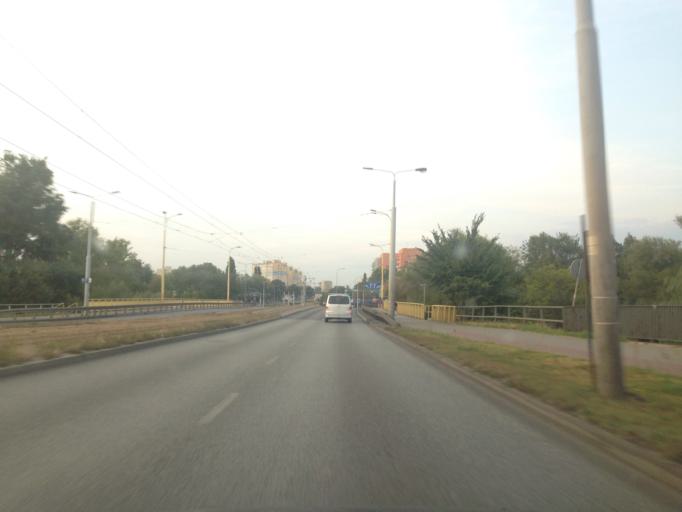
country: PL
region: Kujawsko-Pomorskie
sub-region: Bydgoszcz
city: Bydgoszcz
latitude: 53.1186
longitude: 18.0344
